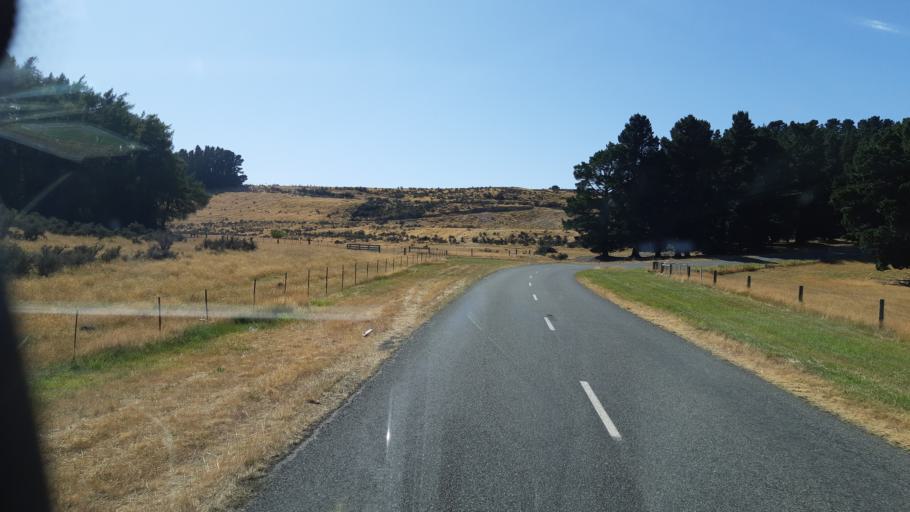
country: NZ
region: Canterbury
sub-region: Ashburton District
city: Methven
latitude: -43.4439
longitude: 171.6291
